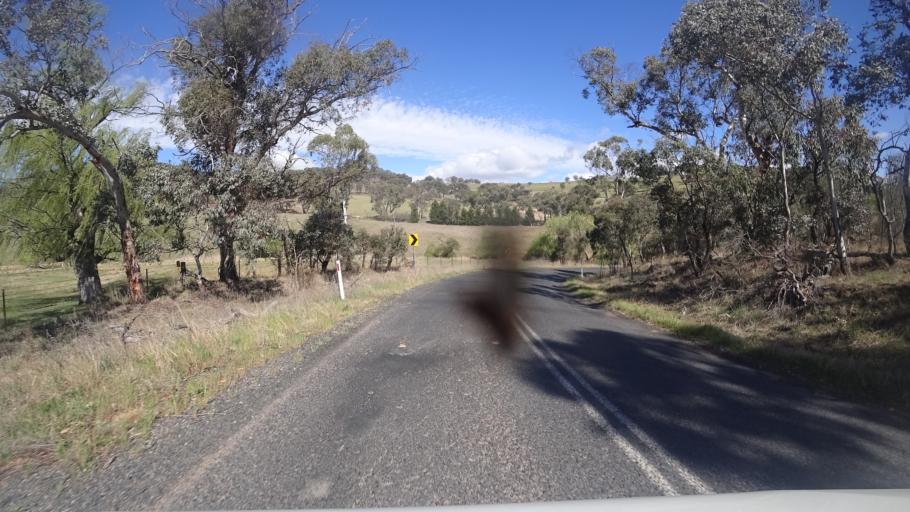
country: AU
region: New South Wales
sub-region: Lithgow
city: Portland
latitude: -33.5236
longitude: 149.9375
